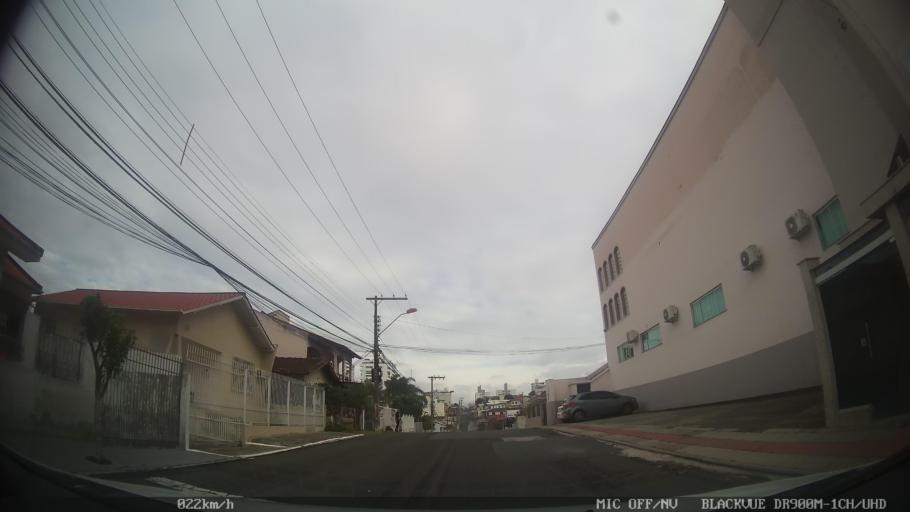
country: BR
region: Santa Catarina
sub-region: Sao Jose
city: Campinas
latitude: -27.5770
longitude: -48.6031
